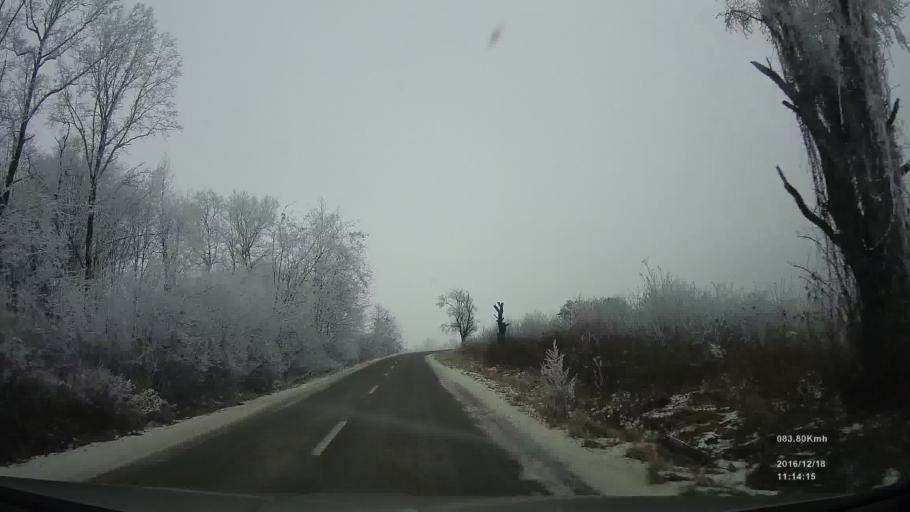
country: SK
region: Presovsky
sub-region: Okres Presov
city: Presov
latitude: 48.8916
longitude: 21.3159
